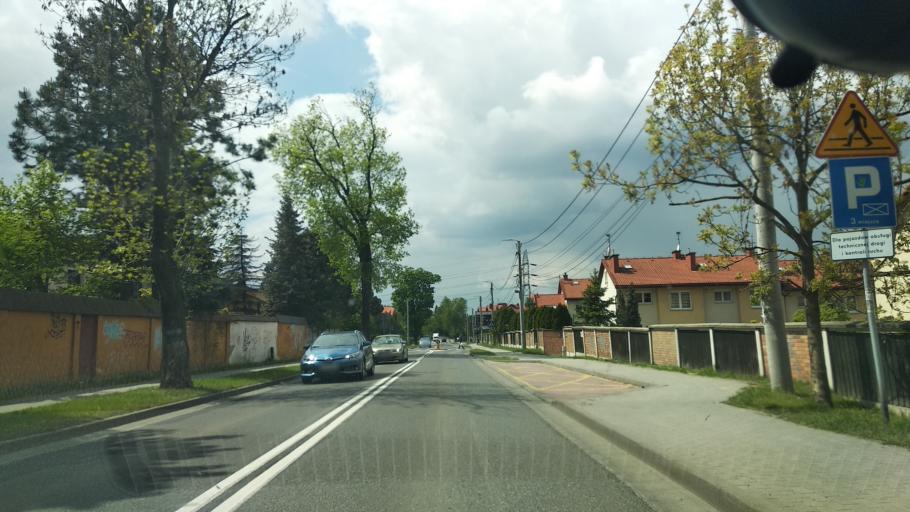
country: PL
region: Silesian Voivodeship
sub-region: Powiat mikolowski
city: Mikolow
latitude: 50.2298
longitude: 18.9462
